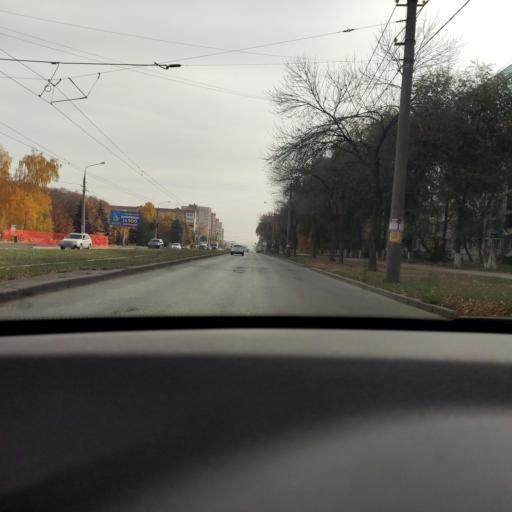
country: RU
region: Samara
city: Samara
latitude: 53.2373
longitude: 50.2173
